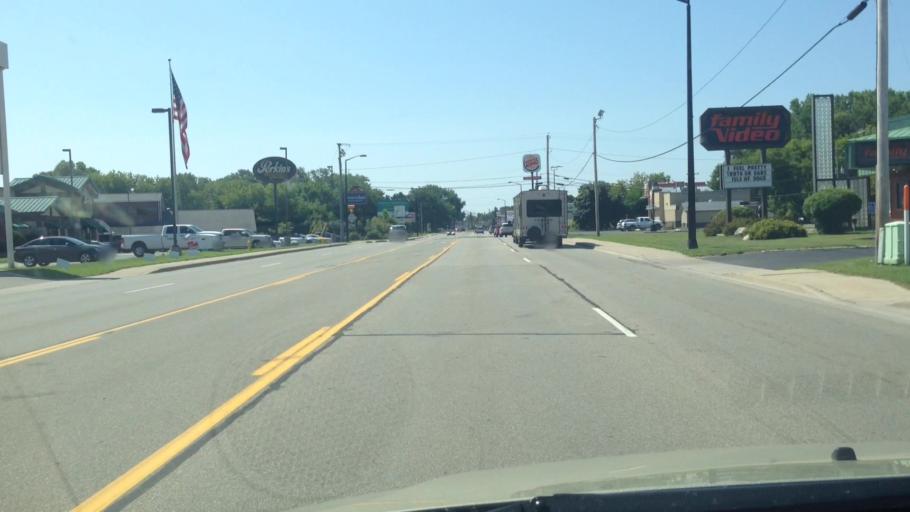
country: US
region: Michigan
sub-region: Menominee County
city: Menominee
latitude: 45.1206
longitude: -87.6135
